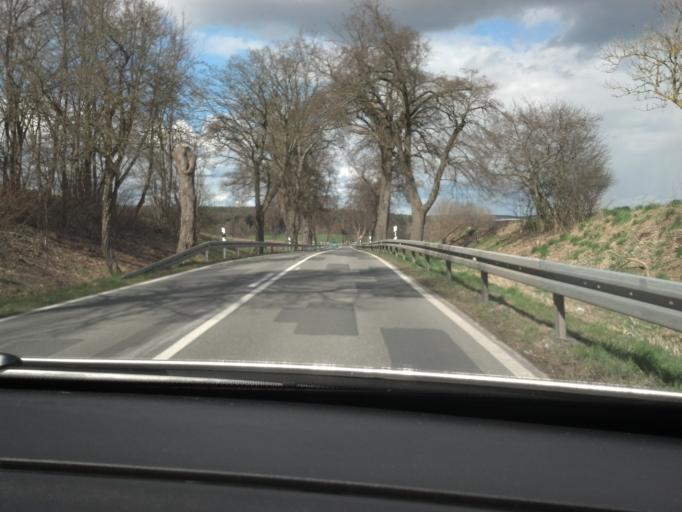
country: DE
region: Mecklenburg-Vorpommern
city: Loitz
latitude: 53.4629
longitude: 13.3596
